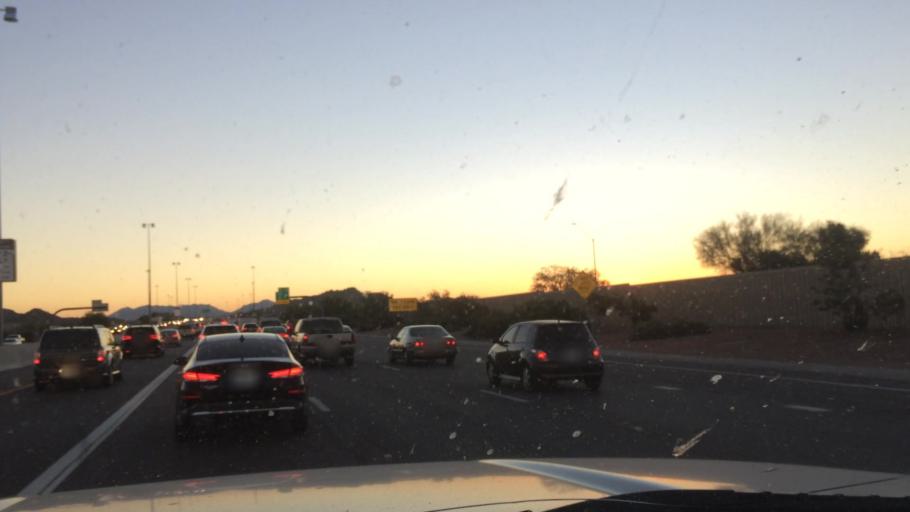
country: US
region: Arizona
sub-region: Maricopa County
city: Glendale
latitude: 33.6680
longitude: -112.0757
